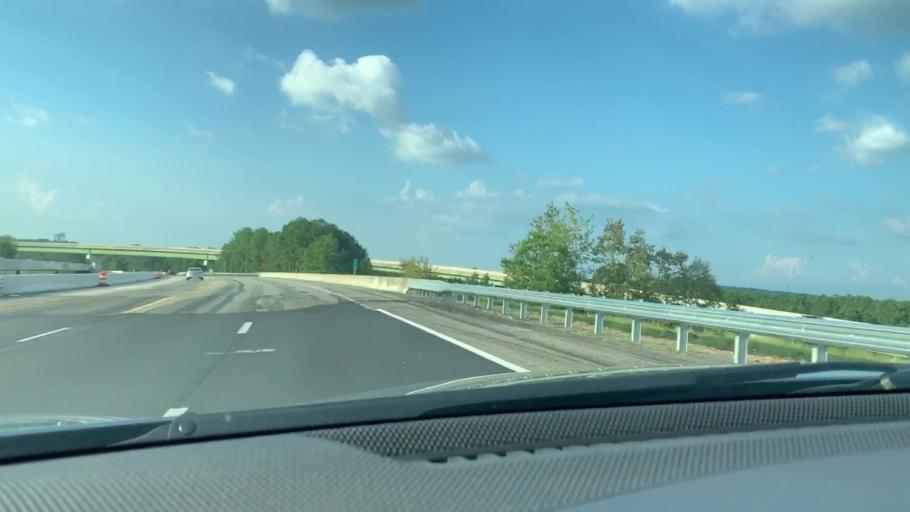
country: US
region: South Carolina
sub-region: Richland County
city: Woodfield
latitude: 34.0669
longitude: -80.9218
